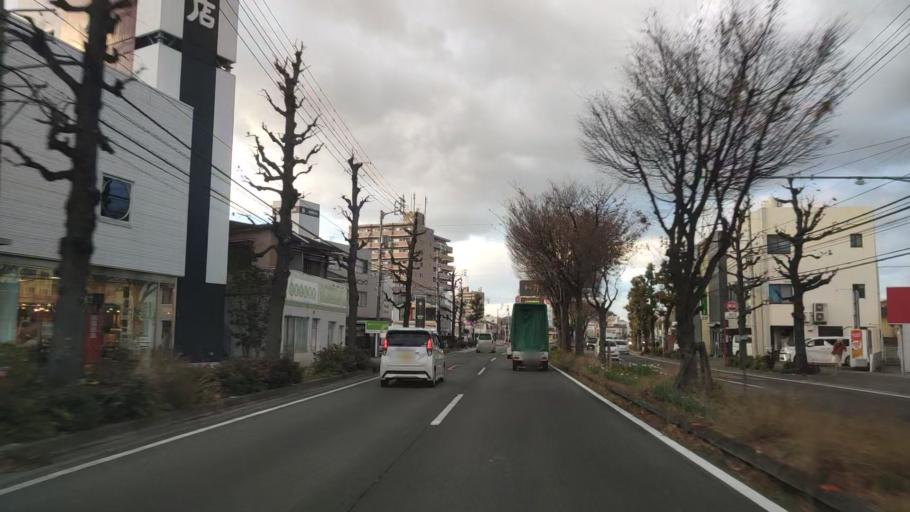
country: JP
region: Ehime
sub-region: Shikoku-chuo Shi
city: Matsuyama
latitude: 33.8148
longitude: 132.7776
